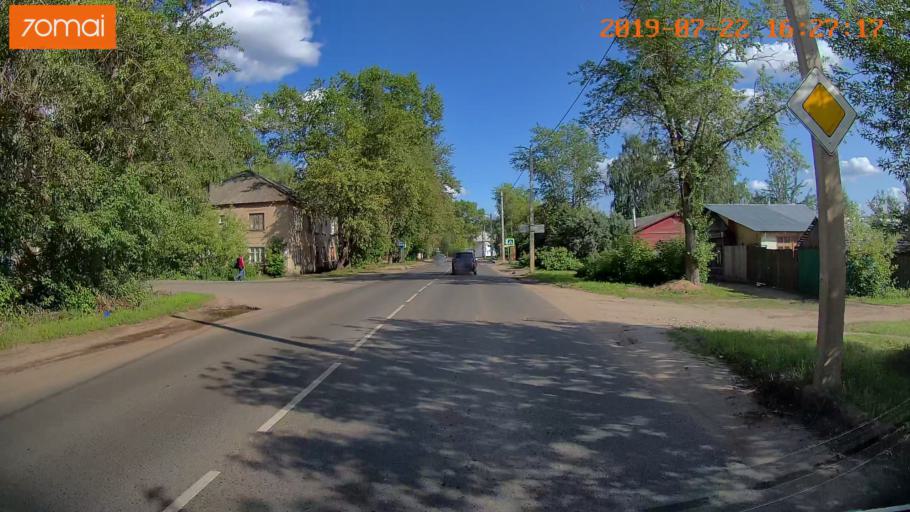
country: RU
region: Ivanovo
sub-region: Gorod Ivanovo
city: Ivanovo
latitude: 57.0447
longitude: 40.9442
